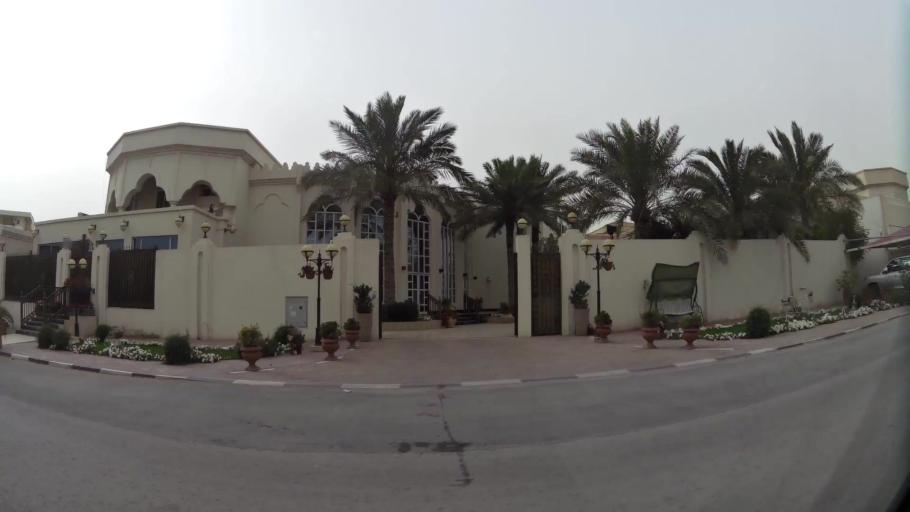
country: QA
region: Baladiyat ad Dawhah
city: Doha
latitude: 25.2501
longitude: 51.4914
